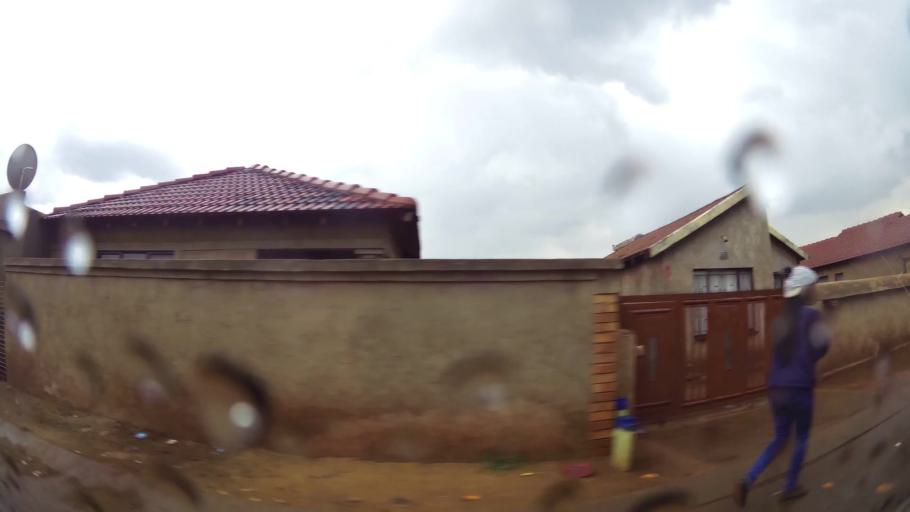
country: ZA
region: Gauteng
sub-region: Ekurhuleni Metropolitan Municipality
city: Germiston
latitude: -26.3633
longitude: 28.1358
